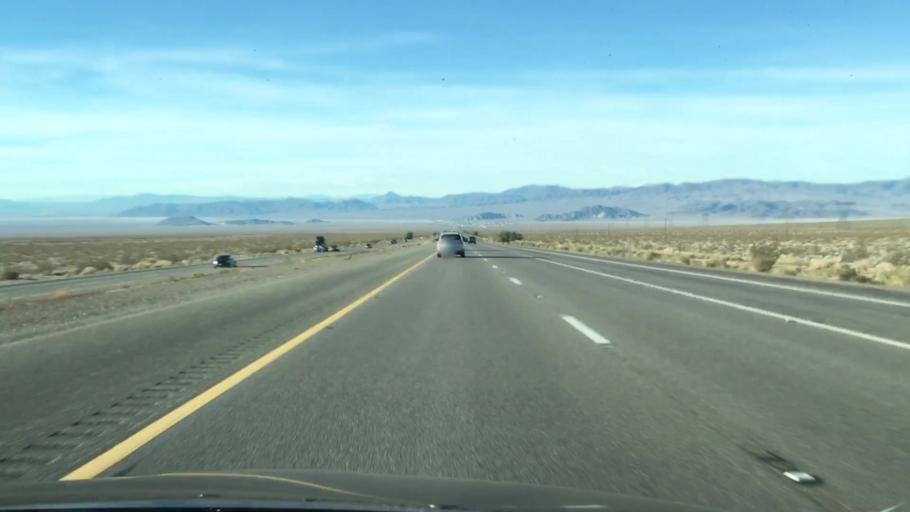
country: US
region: Nevada
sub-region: Clark County
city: Sandy Valley
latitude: 35.3454
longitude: -115.9484
